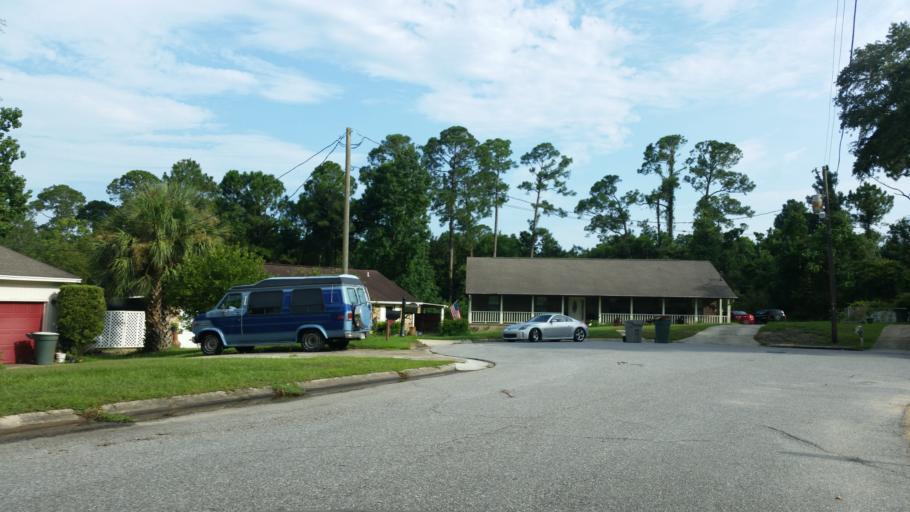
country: US
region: Florida
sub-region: Escambia County
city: Ferry Pass
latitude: 30.5110
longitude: -87.1731
